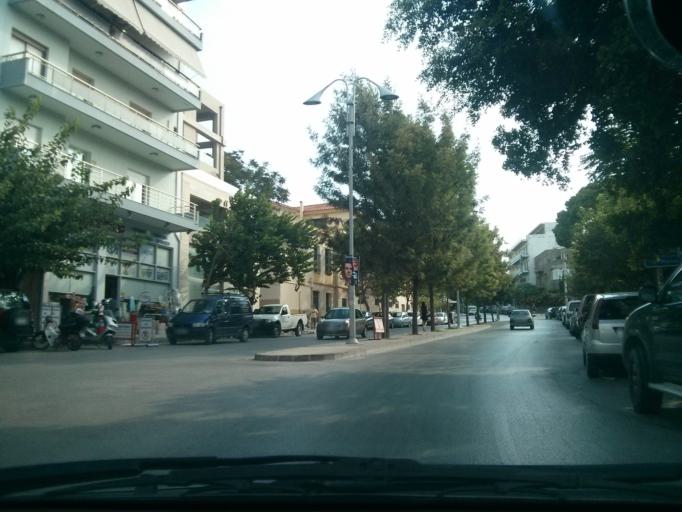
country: GR
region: Crete
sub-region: Nomos Irakleiou
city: Irakleion
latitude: 35.3334
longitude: 25.1351
